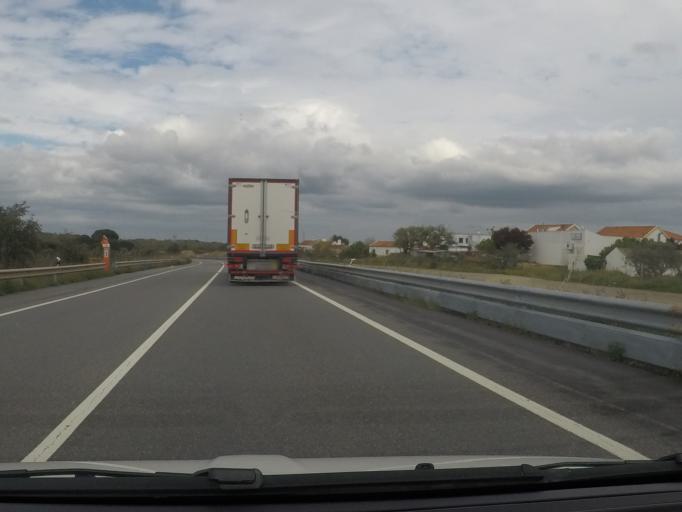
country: PT
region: Setubal
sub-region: Santiago do Cacem
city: Santiago do Cacem
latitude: 38.0728
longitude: -8.6507
